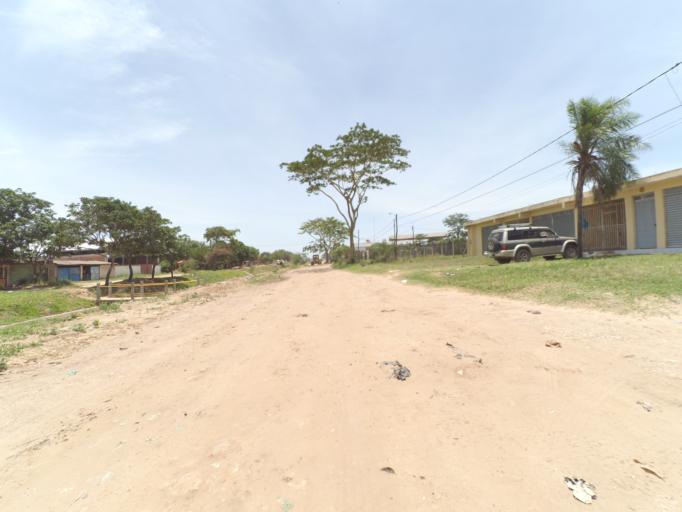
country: BO
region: Santa Cruz
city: Santa Cruz de la Sierra
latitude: -17.8252
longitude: -63.2454
